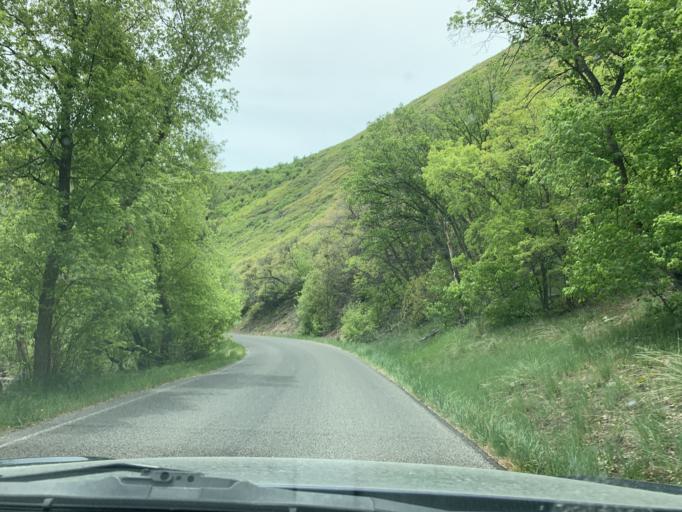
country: US
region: Utah
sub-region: Utah County
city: Mapleton
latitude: 40.1770
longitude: -111.4729
